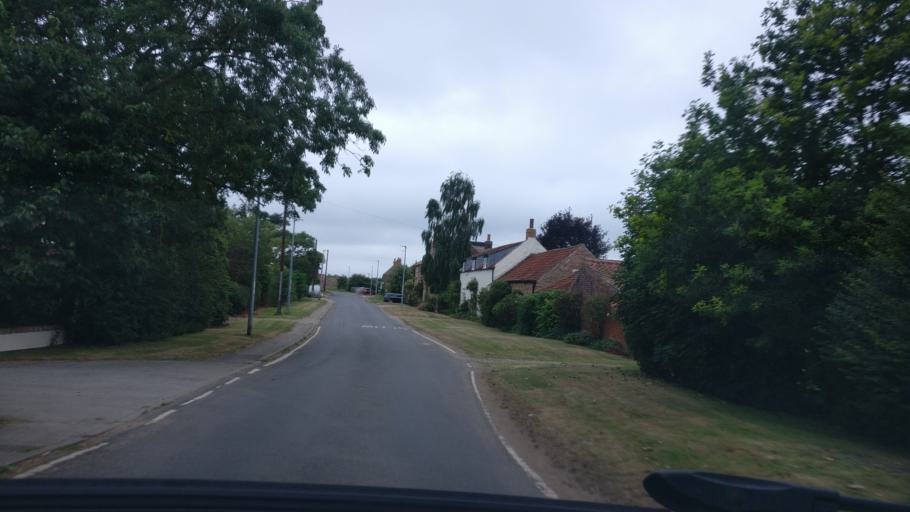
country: GB
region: England
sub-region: East Riding of Yorkshire
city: Leven
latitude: 53.8934
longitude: -0.3257
